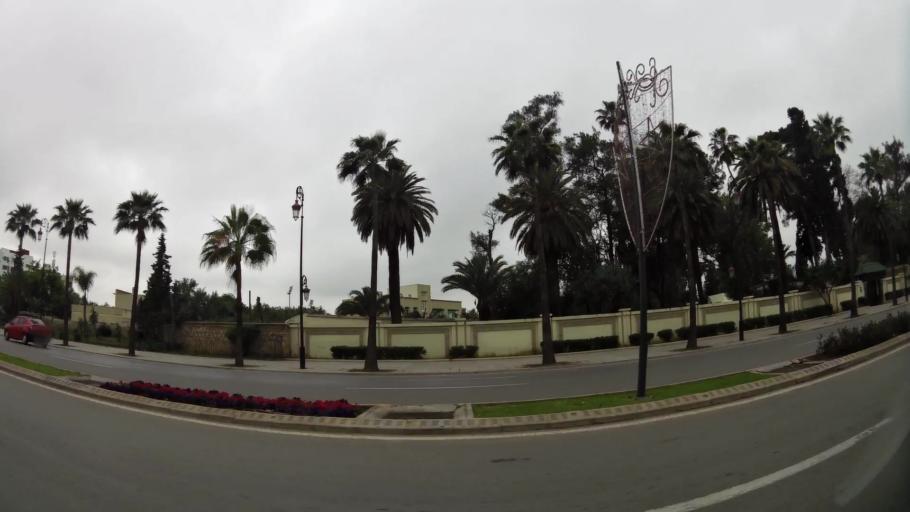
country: MA
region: Fes-Boulemane
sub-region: Fes
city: Fes
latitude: 34.0478
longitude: -4.9961
